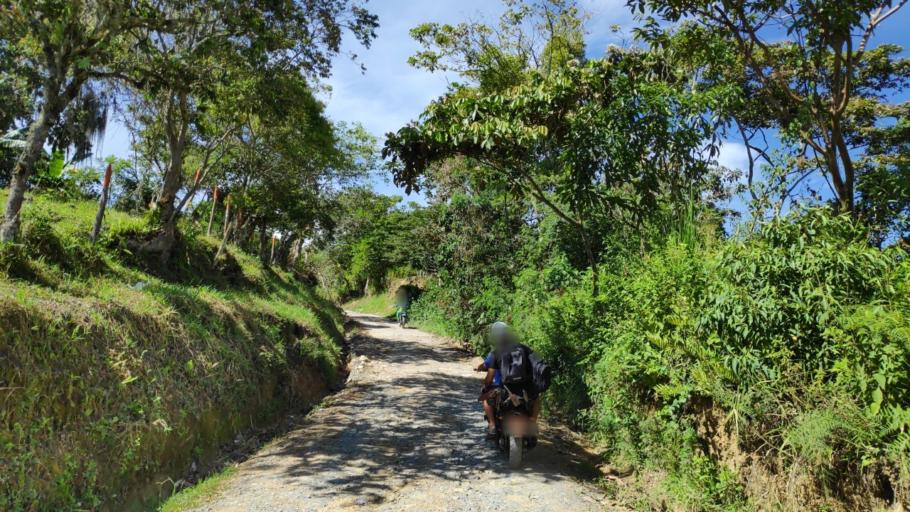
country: CO
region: Santander
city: Guepsa
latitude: 6.0050
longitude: -73.5530
